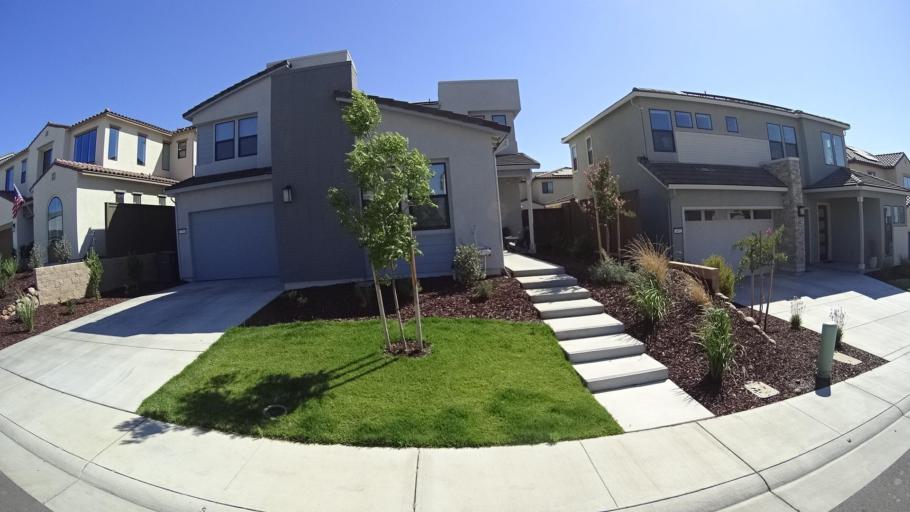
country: US
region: California
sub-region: Placer County
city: Rocklin
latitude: 38.8293
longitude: -121.2611
